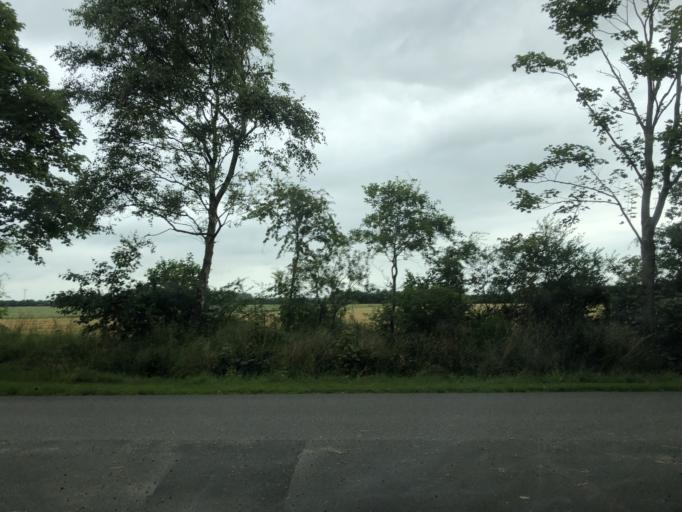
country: DK
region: Central Jutland
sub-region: Herning Kommune
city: Vildbjerg
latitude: 56.1938
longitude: 8.8013
